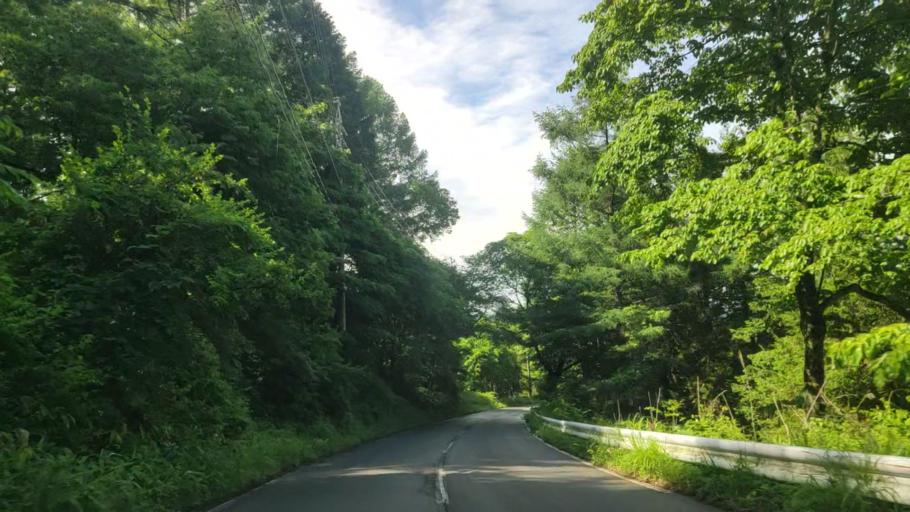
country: JP
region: Nagano
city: Suwa
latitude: 36.0738
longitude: 138.1377
